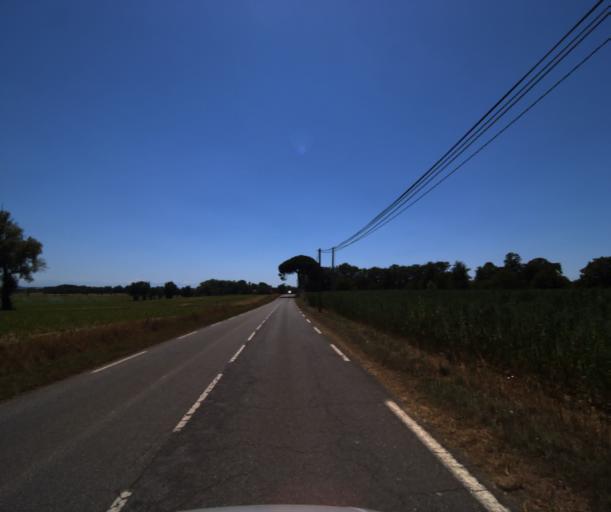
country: FR
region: Midi-Pyrenees
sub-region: Departement de la Haute-Garonne
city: Seysses
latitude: 43.4619
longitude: 1.2973
